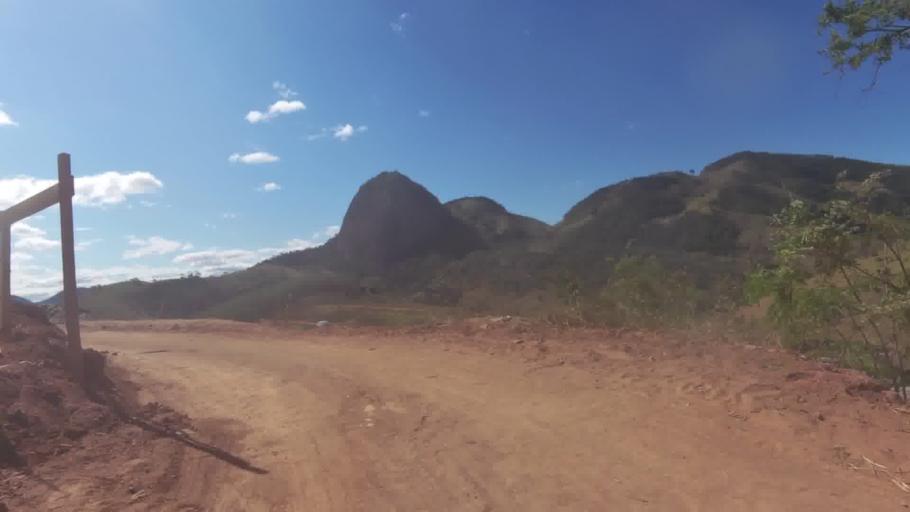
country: BR
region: Espirito Santo
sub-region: Cachoeiro De Itapemirim
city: Cachoeiro de Itapemirim
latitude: -20.9192
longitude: -41.1930
